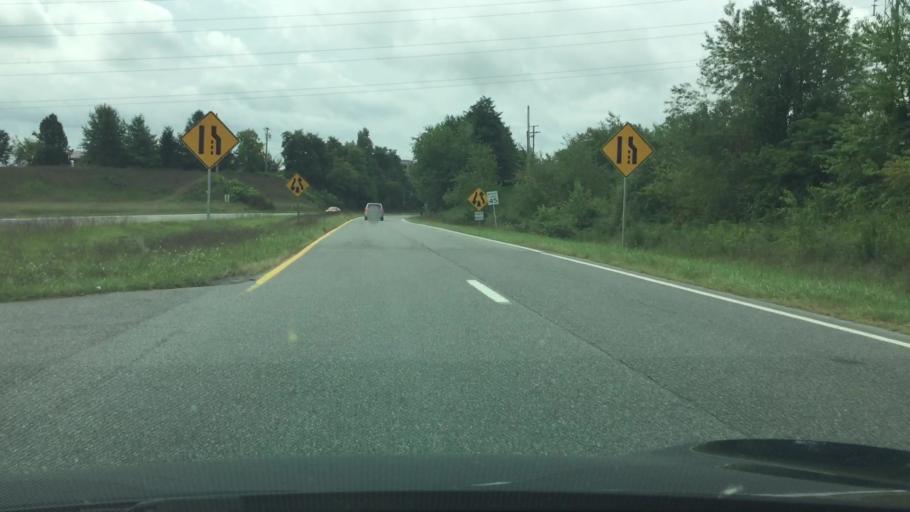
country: US
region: Virginia
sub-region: City of Radford
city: Radford
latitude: 37.0934
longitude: -80.5068
